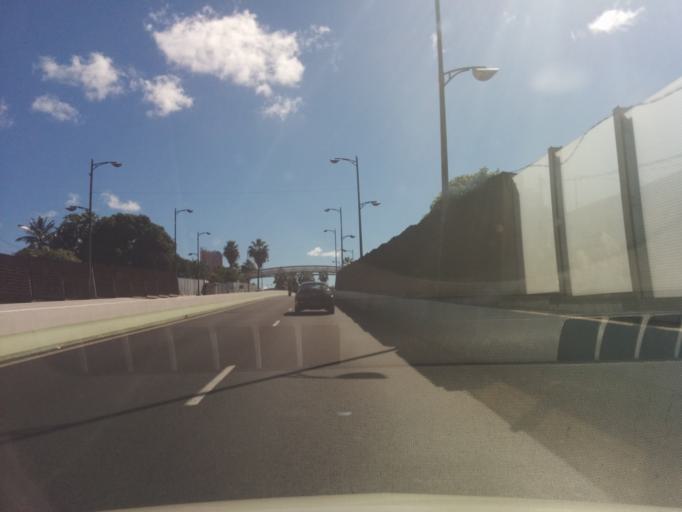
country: MQ
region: Martinique
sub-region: Martinique
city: Fort-de-France
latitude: 14.6060
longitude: -61.0921
